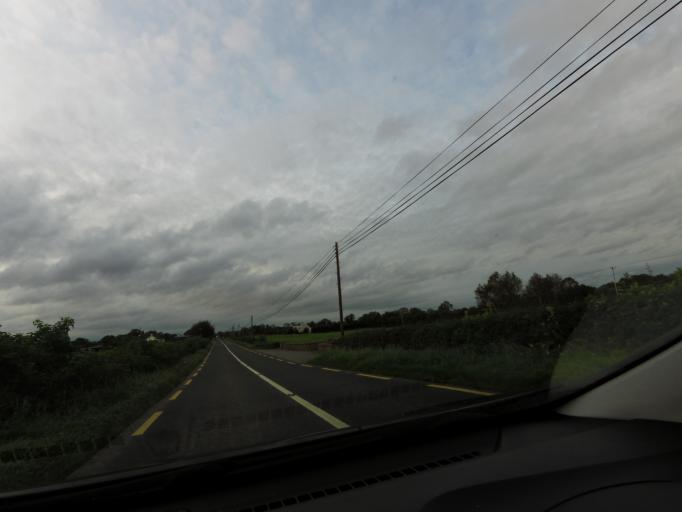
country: IE
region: Leinster
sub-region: Uibh Fhaili
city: Ferbane
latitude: 53.3658
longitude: -7.8542
